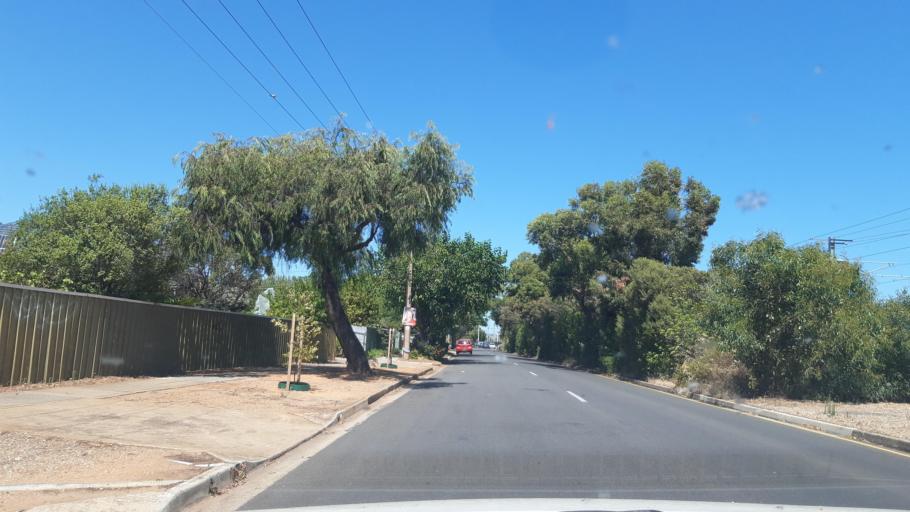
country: AU
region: South Australia
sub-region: Mitcham
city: Clarence Gardens
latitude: -34.9811
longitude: 138.5685
